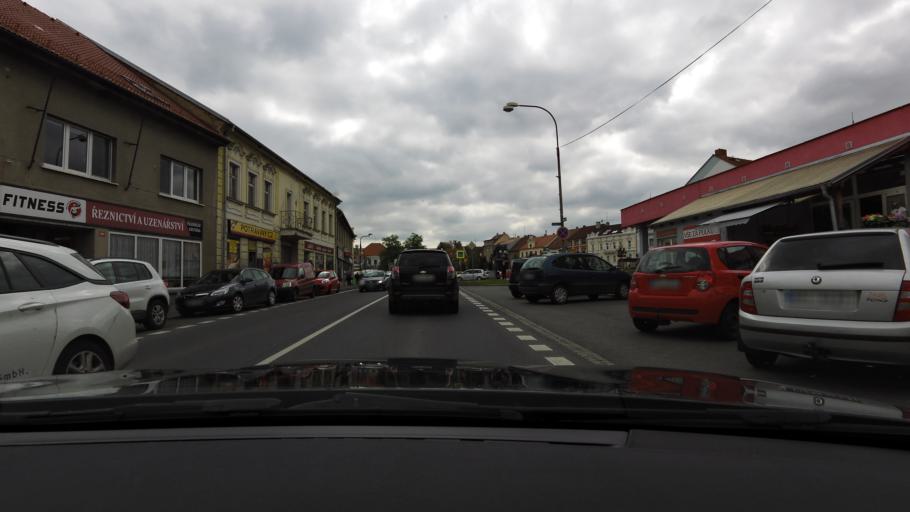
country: CZ
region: Plzensky
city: Prestice
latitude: 49.5734
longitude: 13.3312
